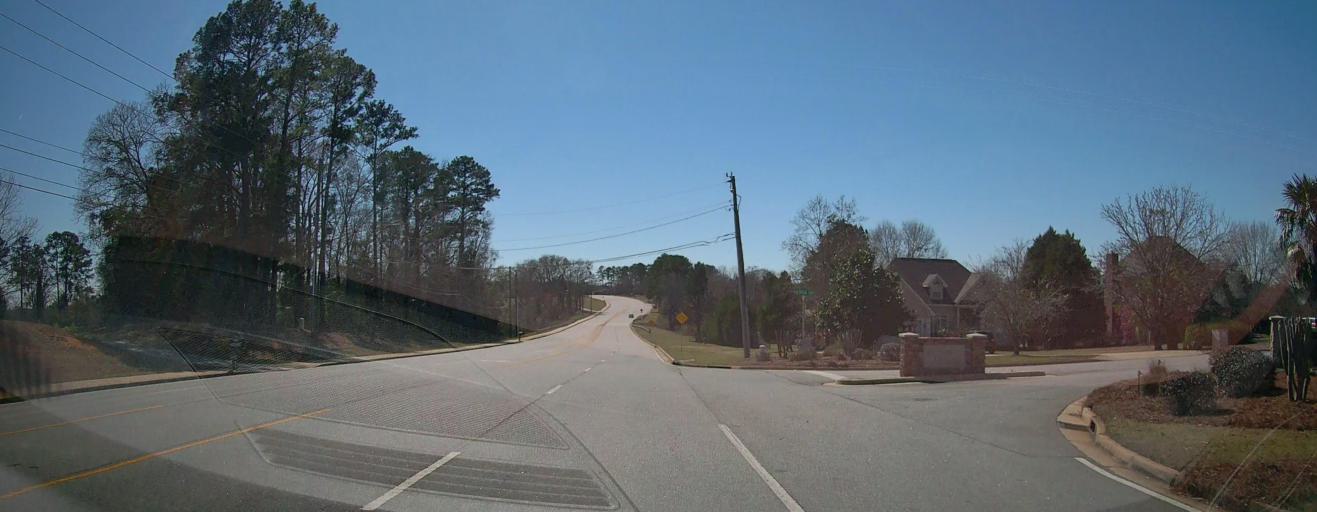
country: US
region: Georgia
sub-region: Houston County
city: Robins Air Force Base
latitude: 32.5196
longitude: -83.6429
